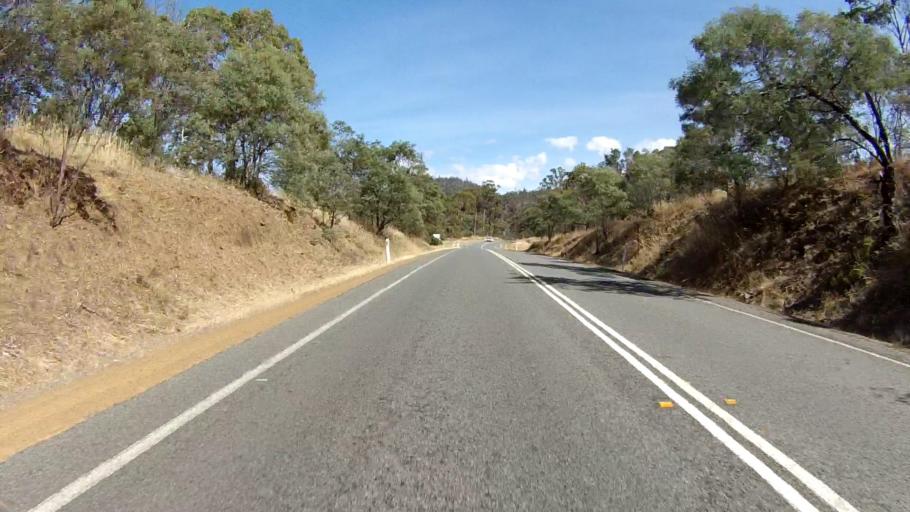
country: AU
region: Tasmania
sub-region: Sorell
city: Sorell
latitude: -42.6069
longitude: 147.6716
